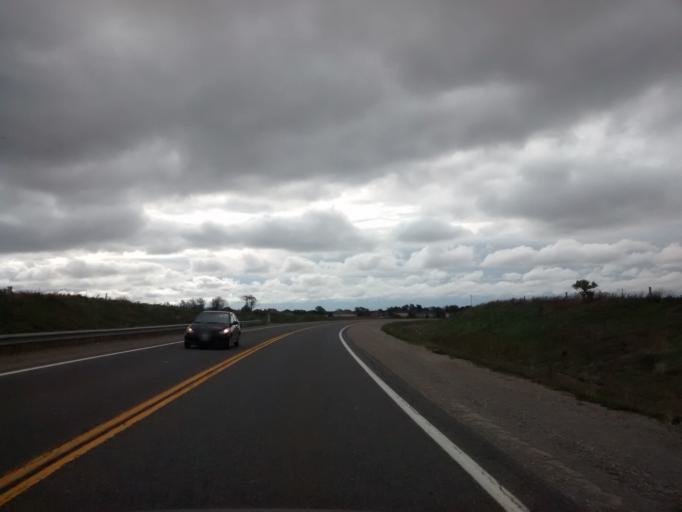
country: CA
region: Ontario
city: Ancaster
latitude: 43.1534
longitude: -79.9293
